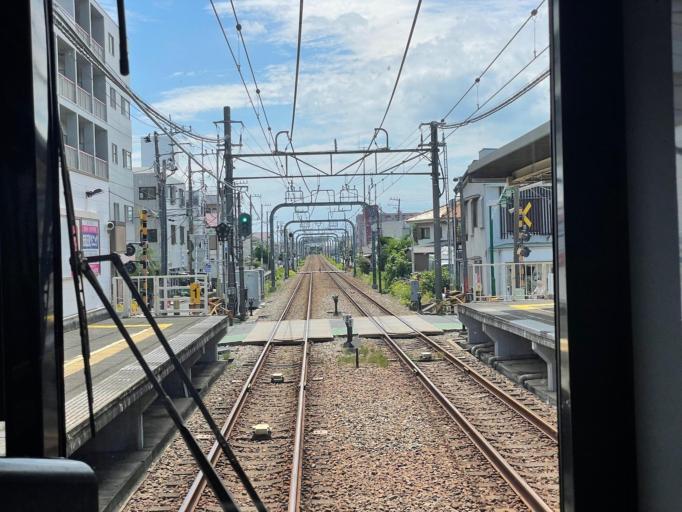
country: JP
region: Kanagawa
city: Fujisawa
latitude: 35.3311
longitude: 139.4752
